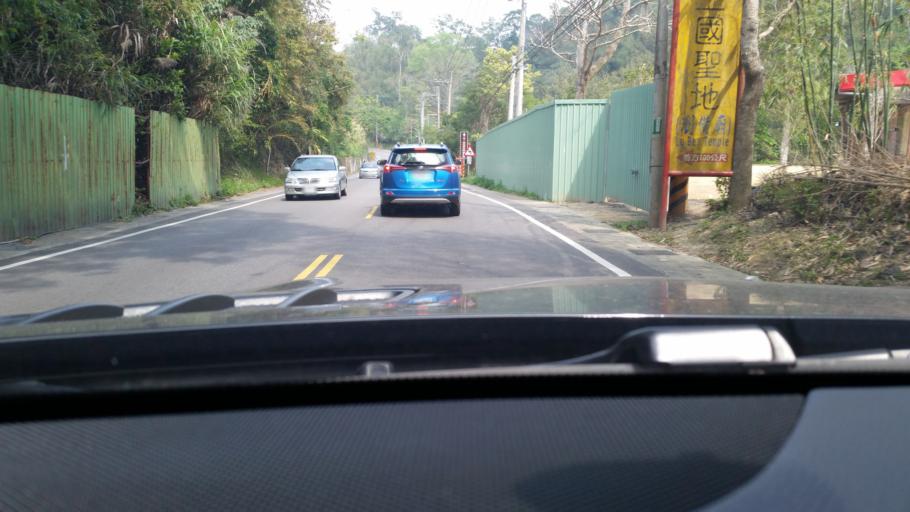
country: TW
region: Taiwan
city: Daxi
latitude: 24.8296
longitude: 121.3179
